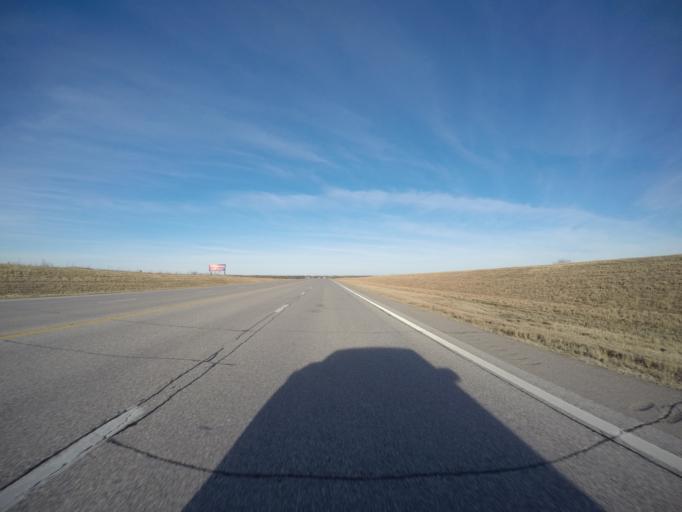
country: US
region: Kansas
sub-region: Marion County
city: Peabody
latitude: 38.1544
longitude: -97.2143
